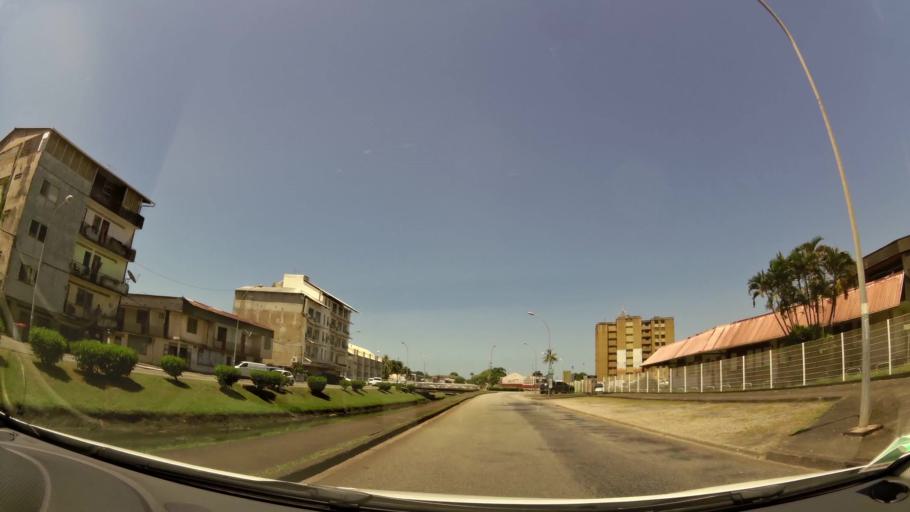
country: GF
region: Guyane
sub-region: Guyane
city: Cayenne
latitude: 4.9368
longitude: -52.3269
